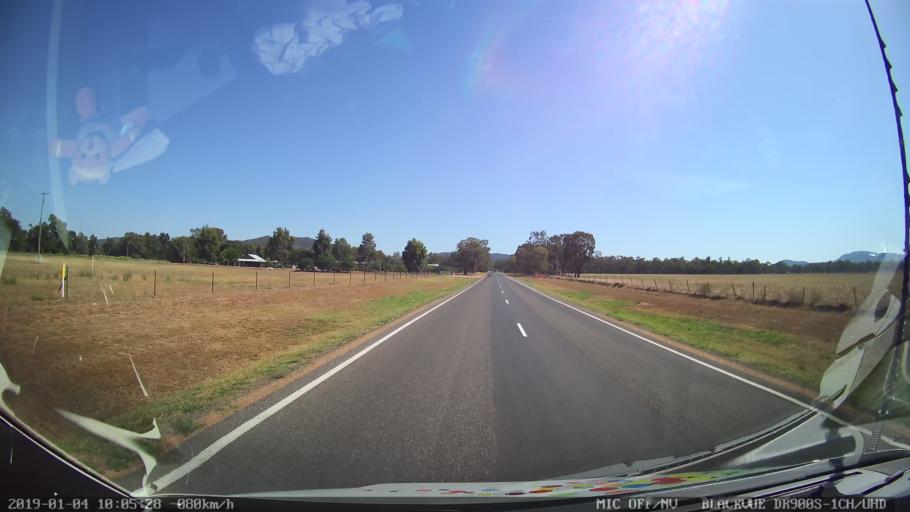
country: AU
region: New South Wales
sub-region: Cabonne
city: Canowindra
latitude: -33.4414
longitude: 148.3653
